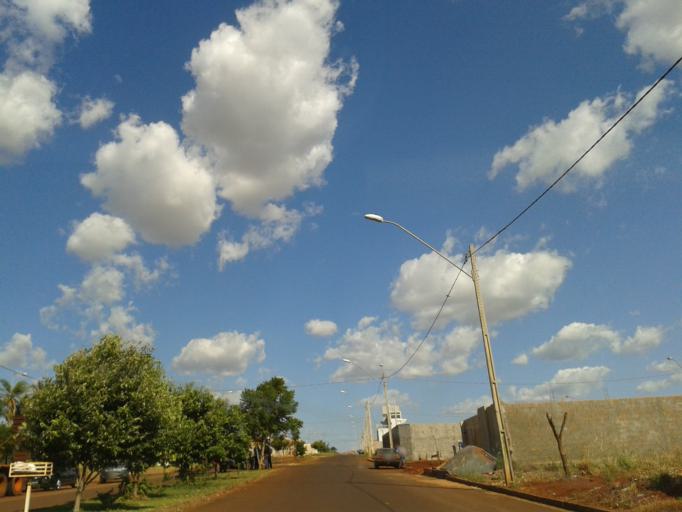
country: BR
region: Minas Gerais
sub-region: Capinopolis
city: Capinopolis
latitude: -18.6893
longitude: -49.5762
